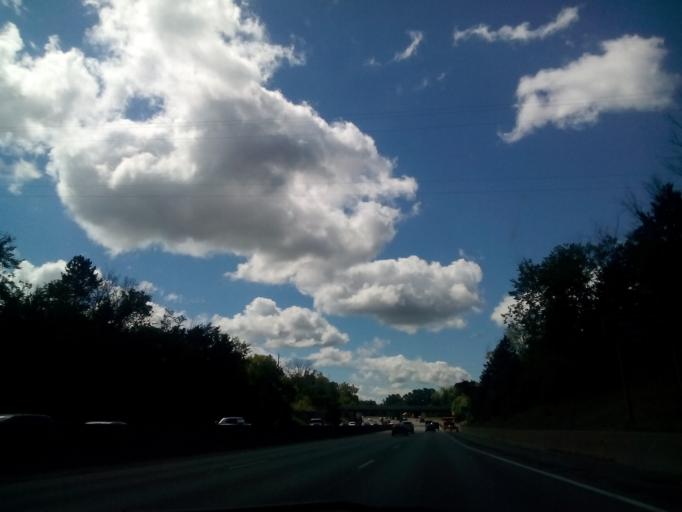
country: US
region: Michigan
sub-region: Genesee County
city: Flint
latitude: 43.0009
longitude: -83.7496
